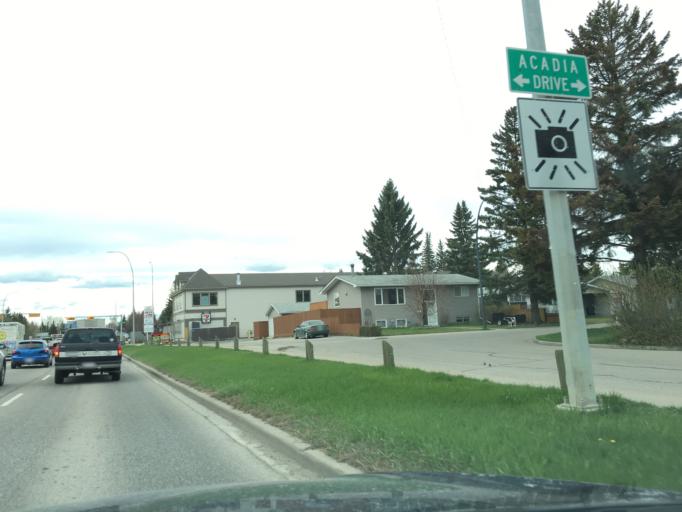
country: CA
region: Alberta
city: Calgary
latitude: 50.9641
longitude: -114.0467
